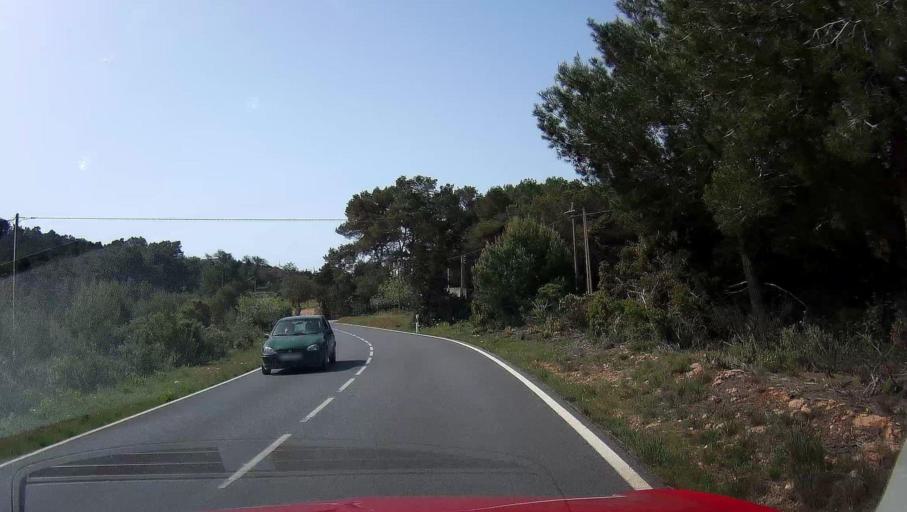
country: ES
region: Balearic Islands
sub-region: Illes Balears
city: Sant Joan de Labritja
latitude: 39.0415
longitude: 1.5661
